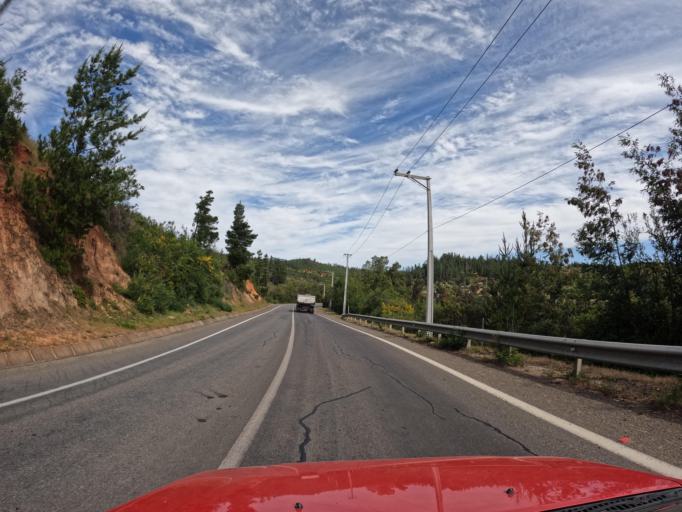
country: CL
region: Maule
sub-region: Provincia de Talca
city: Talca
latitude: -35.1691
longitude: -71.9728
